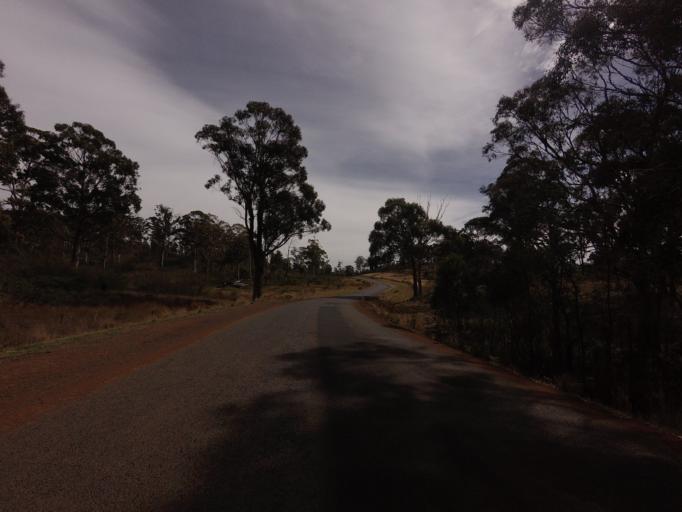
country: AU
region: Tasmania
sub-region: Sorell
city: Sorell
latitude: -42.5589
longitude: 147.6795
